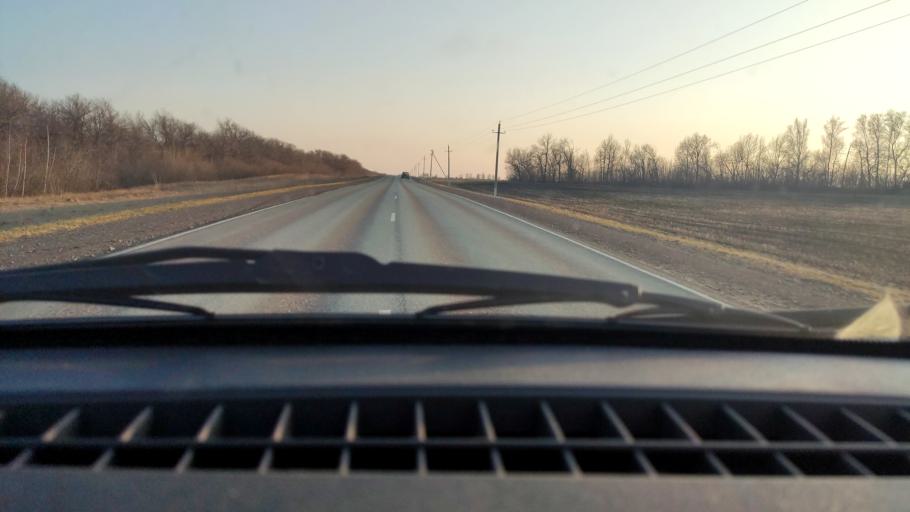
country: RU
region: Bashkortostan
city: Davlekanovo
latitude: 54.3187
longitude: 55.1533
